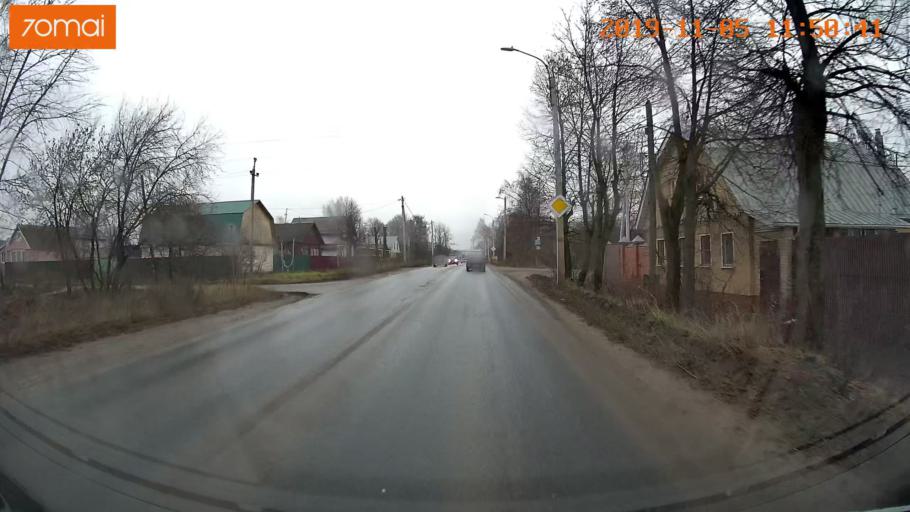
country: RU
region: Ivanovo
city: Bogorodskoye
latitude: 57.0071
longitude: 41.0202
